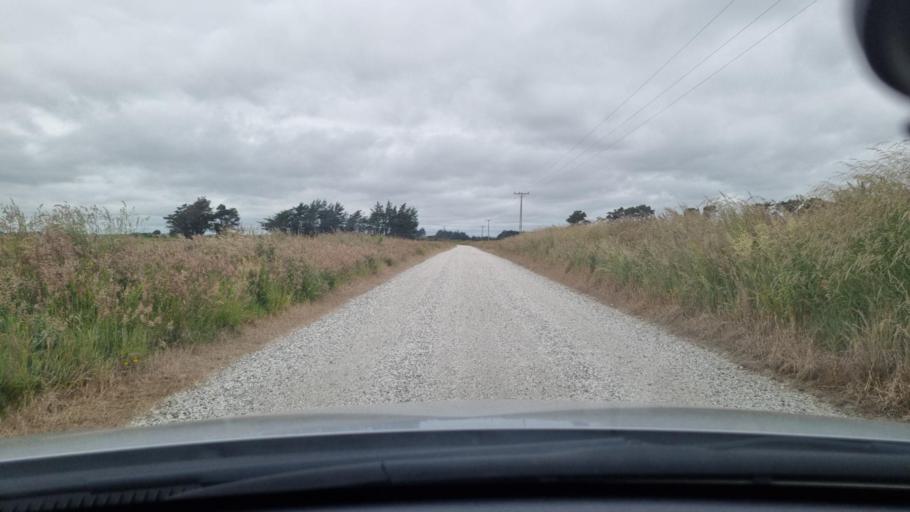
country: NZ
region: Southland
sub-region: Invercargill City
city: Invercargill
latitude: -46.3885
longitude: 168.2785
